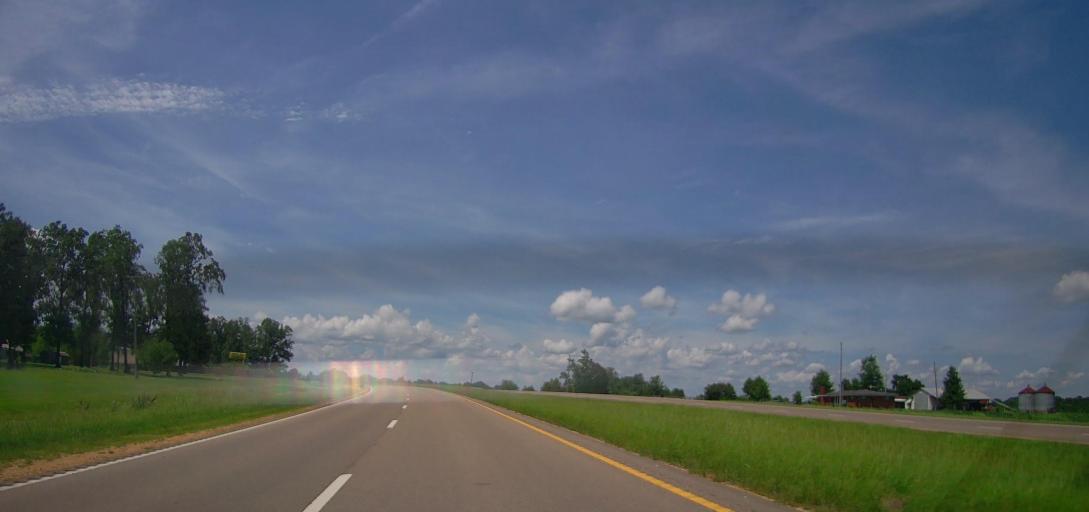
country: US
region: Mississippi
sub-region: Lee County
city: Nettleton
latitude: 33.9756
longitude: -88.6140
